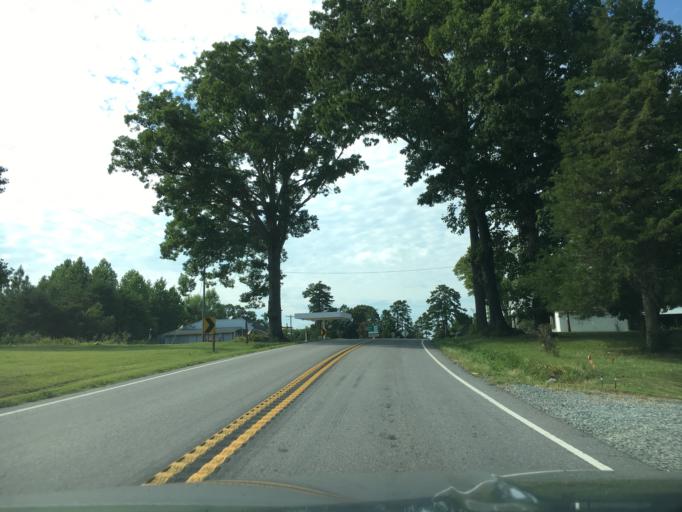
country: US
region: Virginia
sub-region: Halifax County
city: Mountain Road
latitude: 36.8755
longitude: -79.0149
